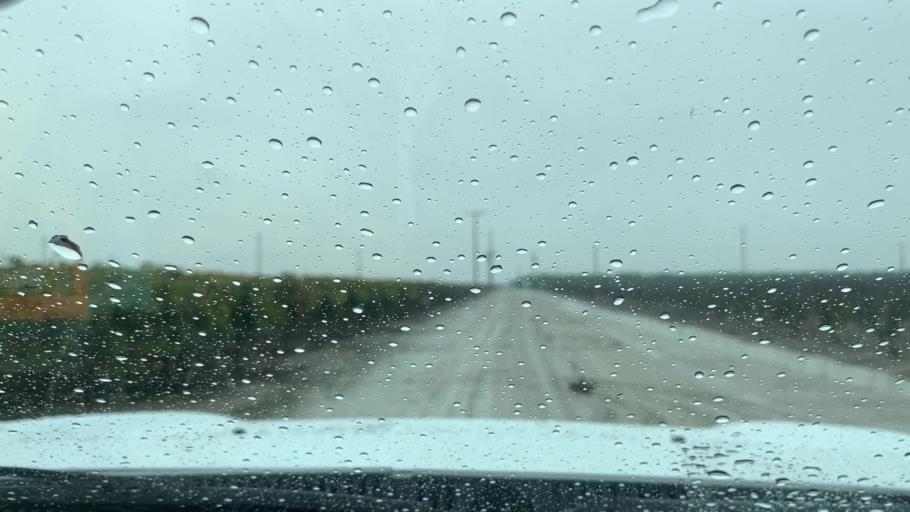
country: US
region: California
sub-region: Tulare County
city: Richgrove
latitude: 35.8364
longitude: -119.1701
